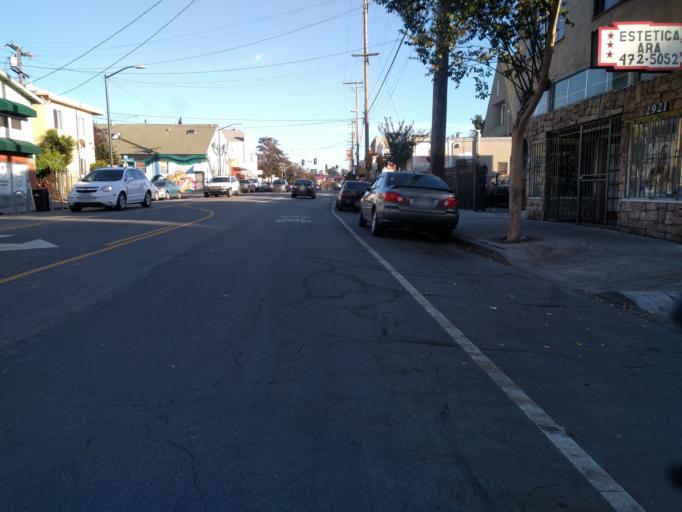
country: US
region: California
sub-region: Alameda County
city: Alameda
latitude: 37.7842
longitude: -122.2242
